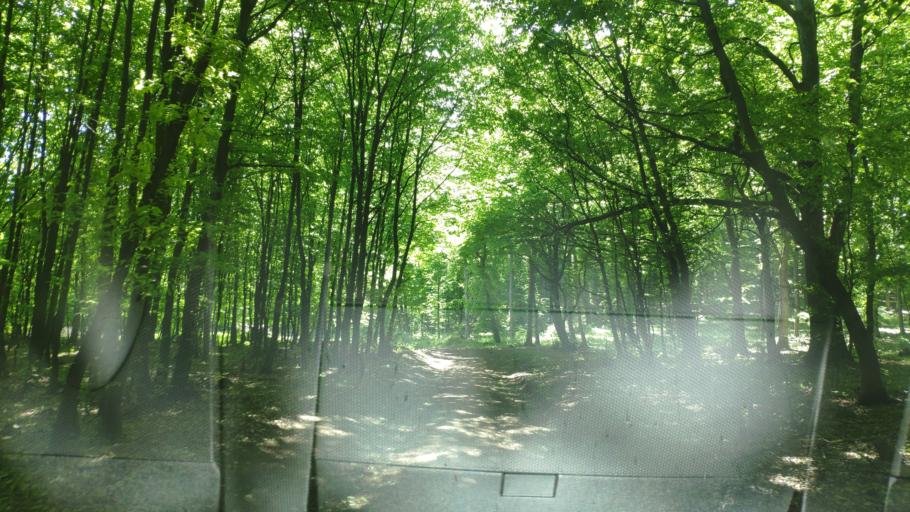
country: SK
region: Kosicky
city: Secovce
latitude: 48.7169
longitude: 21.5808
